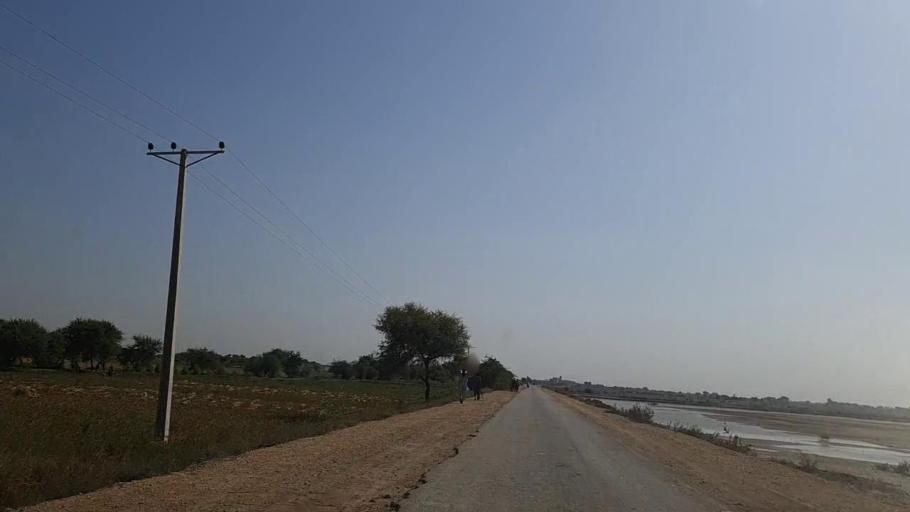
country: PK
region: Sindh
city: Mirpur Batoro
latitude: 24.6278
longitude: 68.2938
